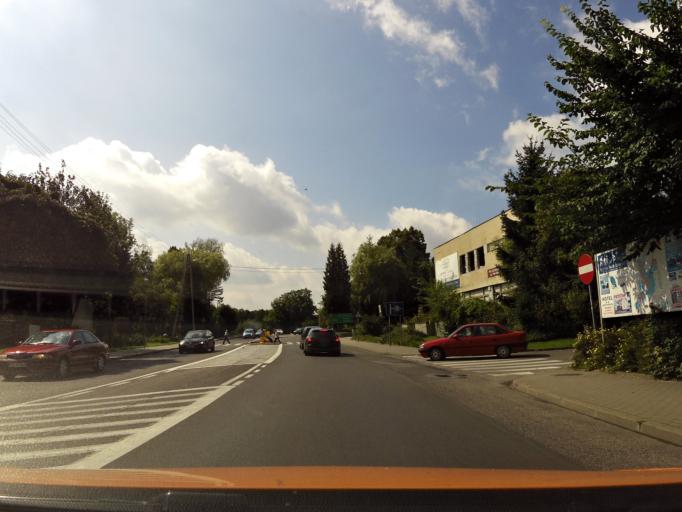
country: PL
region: West Pomeranian Voivodeship
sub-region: Powiat gryficki
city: Ploty
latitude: 53.8026
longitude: 15.2684
